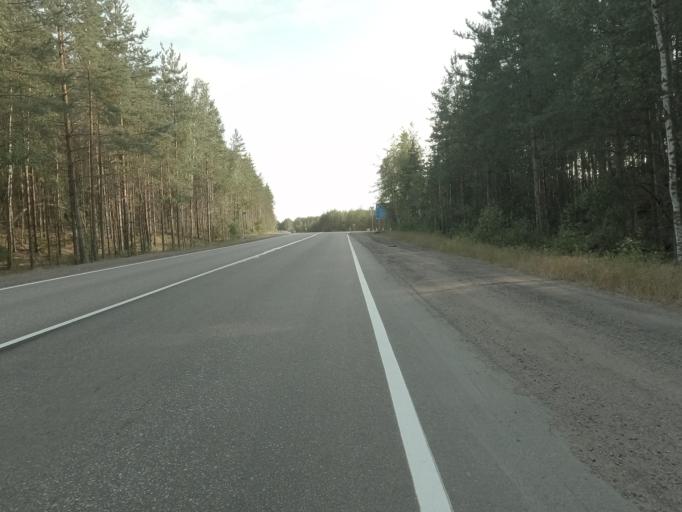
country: RU
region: Leningrad
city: Vyborg
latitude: 60.8356
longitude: 28.8368
